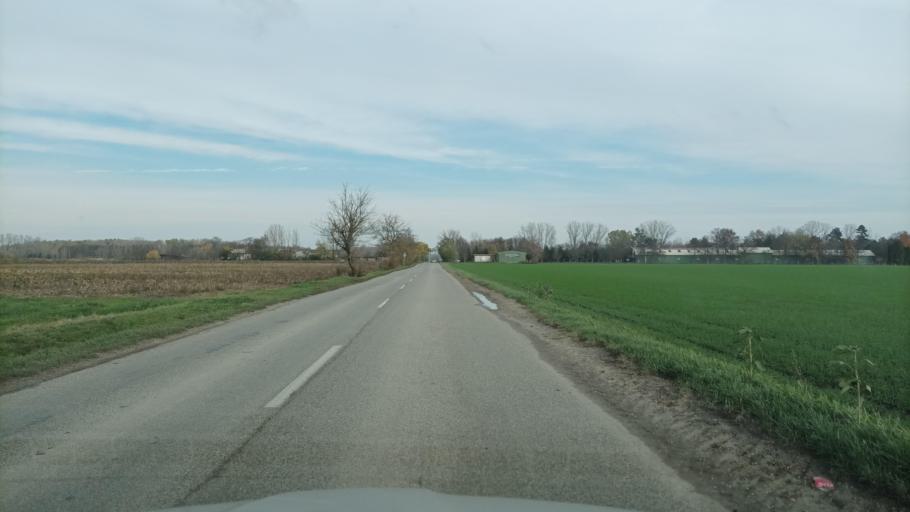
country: HU
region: Pest
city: Rackeve
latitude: 47.1153
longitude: 18.9424
